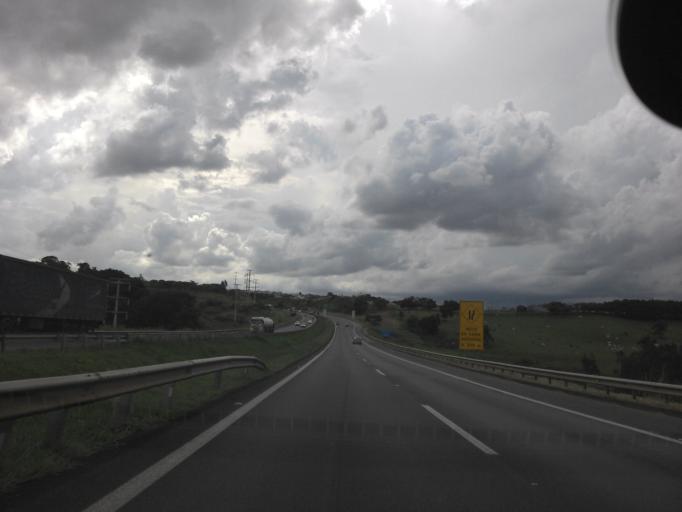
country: BR
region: Sao Paulo
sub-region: Valinhos
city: Valinhos
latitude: -22.9044
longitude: -46.9787
